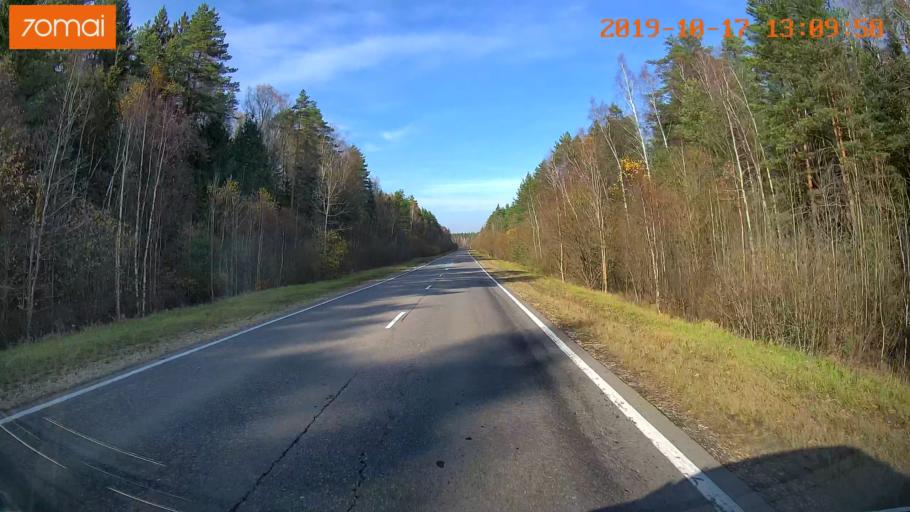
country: RU
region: Rjazan
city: Syntul
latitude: 55.0117
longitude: 41.2597
